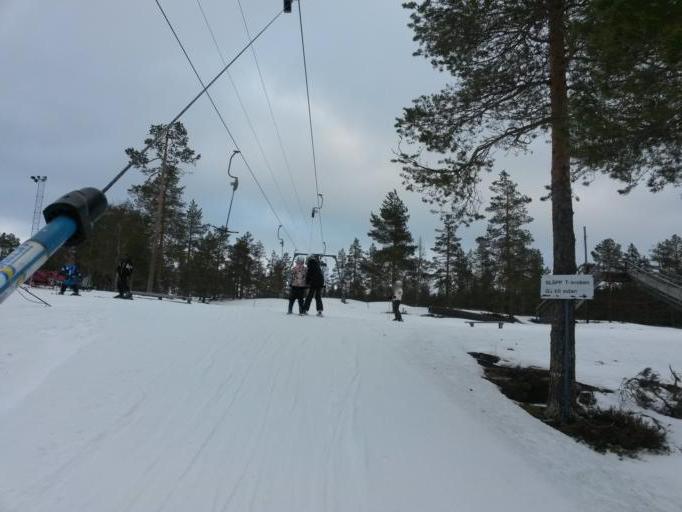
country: SE
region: Vaesterbotten
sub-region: Skelleftea Kommun
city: Viken
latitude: 64.7226
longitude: 20.7873
